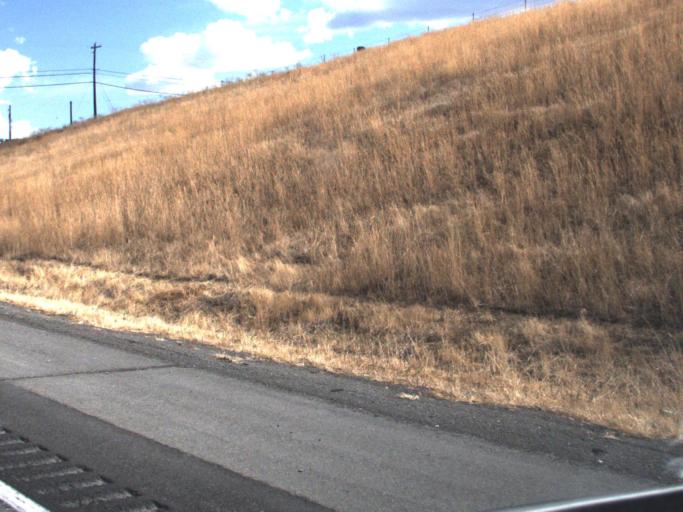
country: US
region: Washington
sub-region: Yakima County
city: Zillah
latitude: 46.3944
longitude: -120.2472
